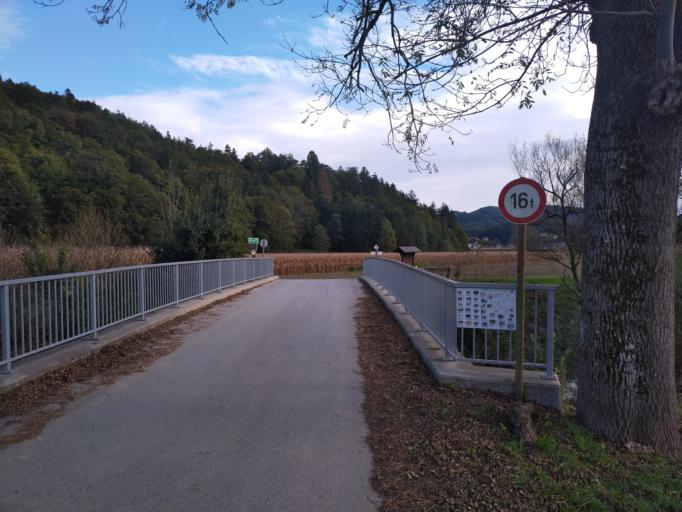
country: AT
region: Styria
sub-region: Politischer Bezirk Leibnitz
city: Grossklein
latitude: 46.7479
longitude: 15.4410
